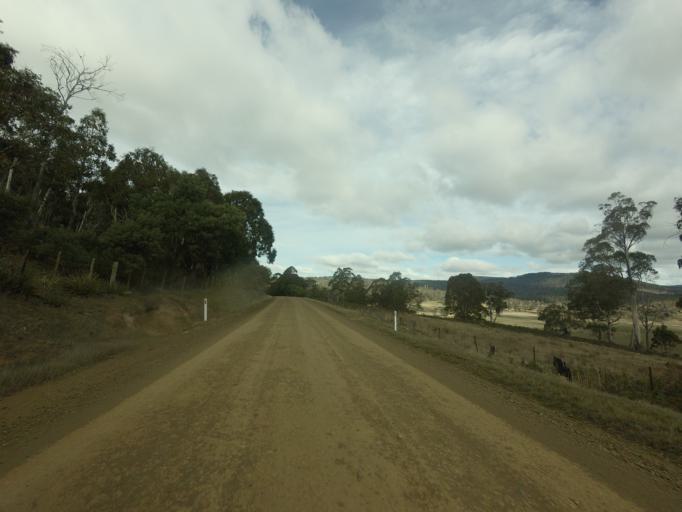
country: AU
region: Tasmania
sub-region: Brighton
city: Bridgewater
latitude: -42.4817
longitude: 147.2969
